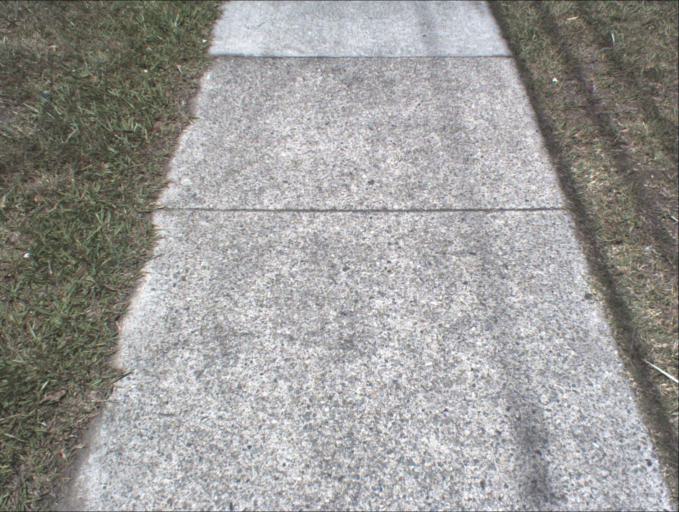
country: AU
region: Queensland
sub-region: Logan
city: Springwood
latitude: -27.6172
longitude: 153.1242
